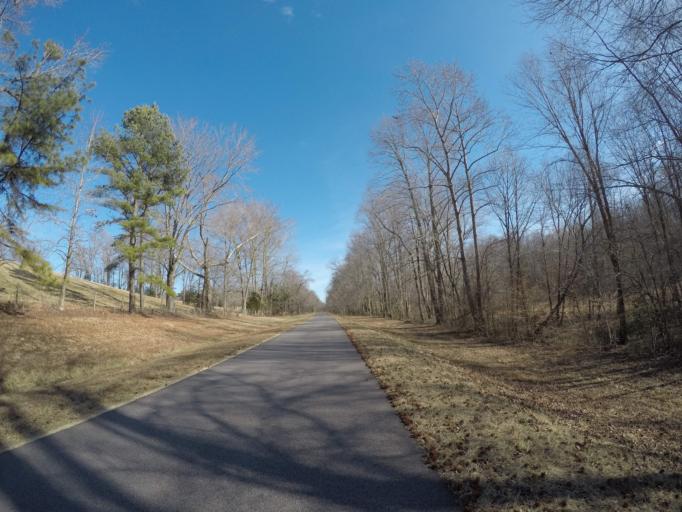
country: US
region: Maryland
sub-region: Charles County
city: Bennsville
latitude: 38.5961
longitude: -77.0000
